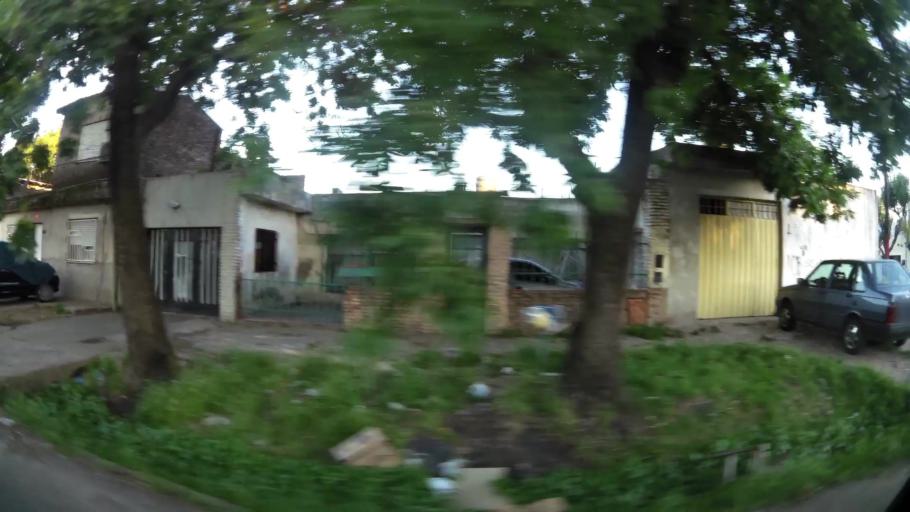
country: AR
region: Santa Fe
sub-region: Departamento de Rosario
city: Rosario
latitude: -32.9646
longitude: -60.6827
